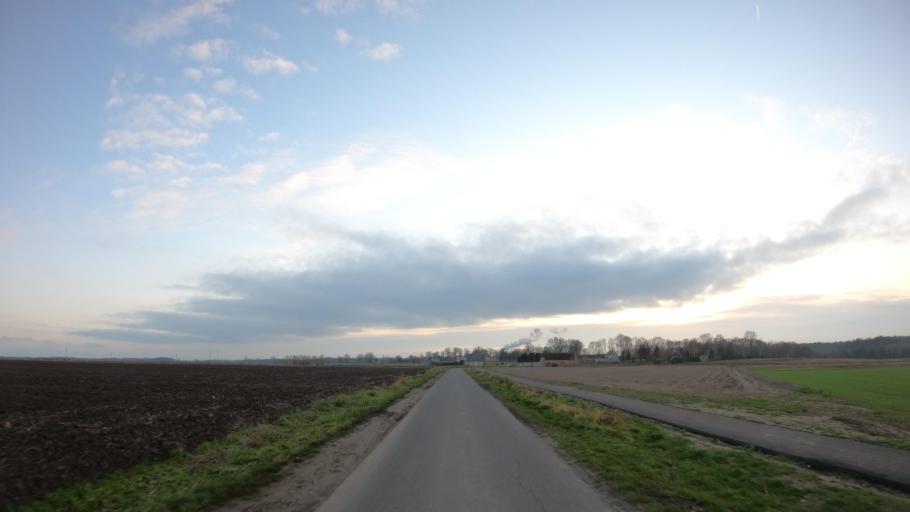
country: PL
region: West Pomeranian Voivodeship
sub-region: Powiat bialogardzki
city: Karlino
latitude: 54.0859
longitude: 15.8839
